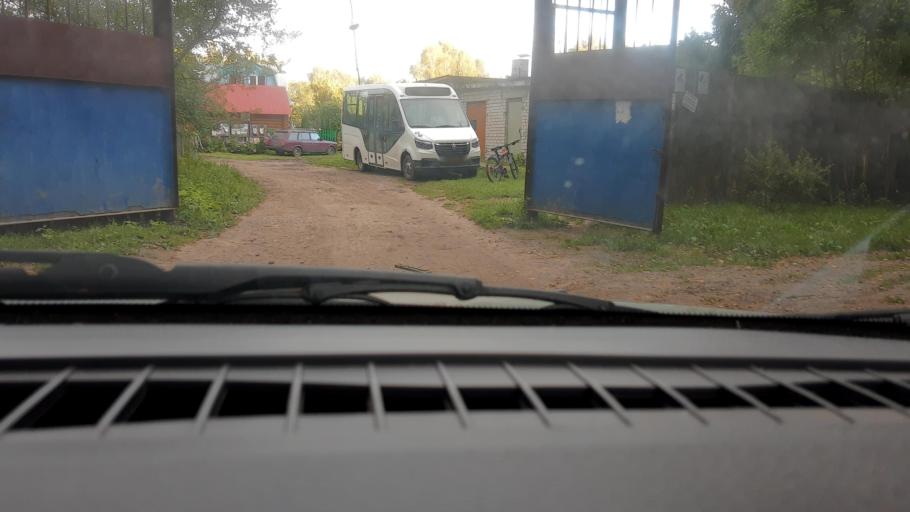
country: RU
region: Nizjnij Novgorod
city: Sitniki
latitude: 56.4506
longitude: 44.0218
